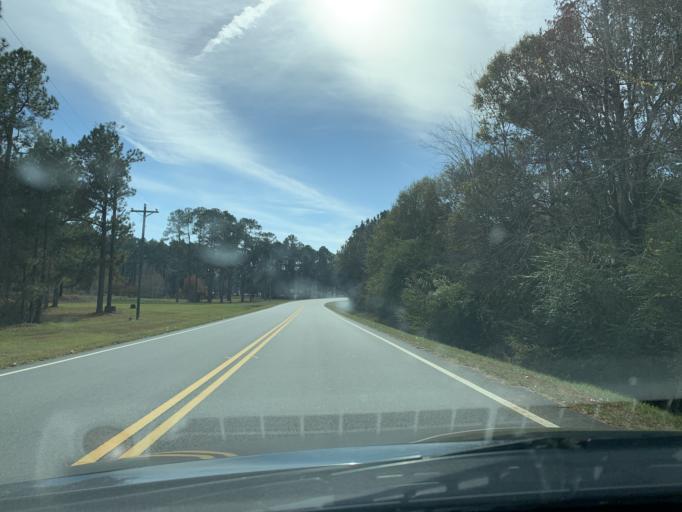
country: US
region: Georgia
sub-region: Turner County
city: Ashburn
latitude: 31.7266
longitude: -83.5818
